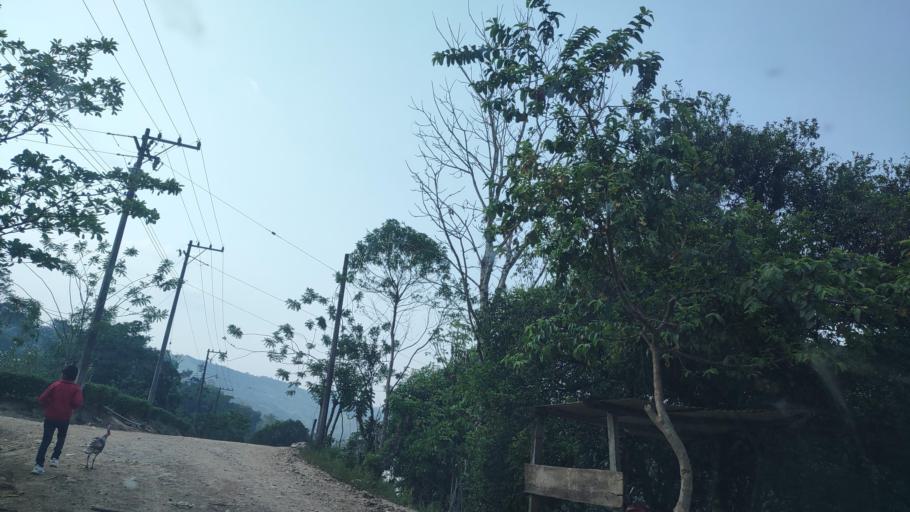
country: MX
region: Chiapas
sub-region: Tecpatan
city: Raudales Malpaso
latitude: 17.3075
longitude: -93.7783
